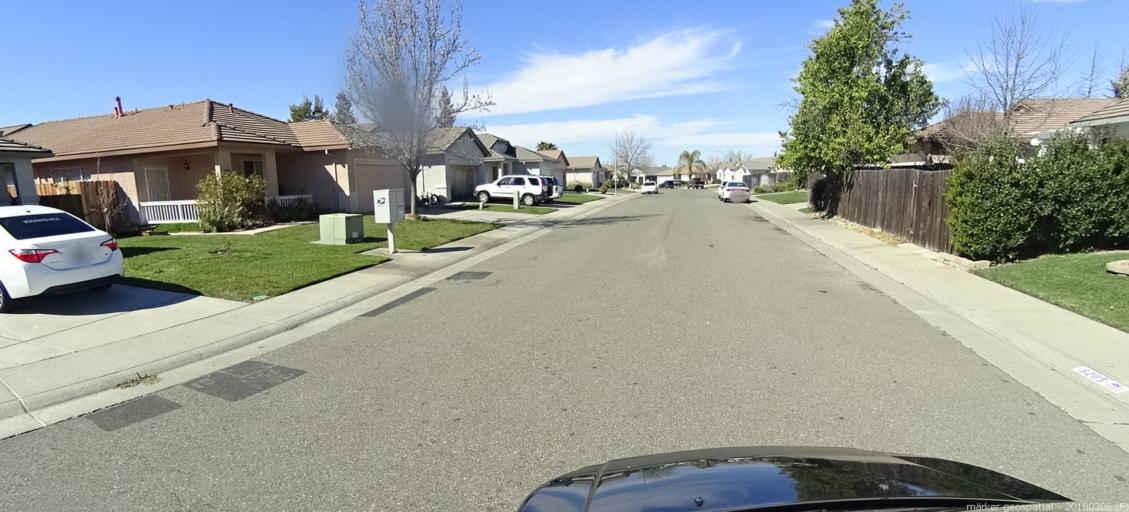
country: US
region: California
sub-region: Sacramento County
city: Vineyard
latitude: 38.4618
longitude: -121.3547
